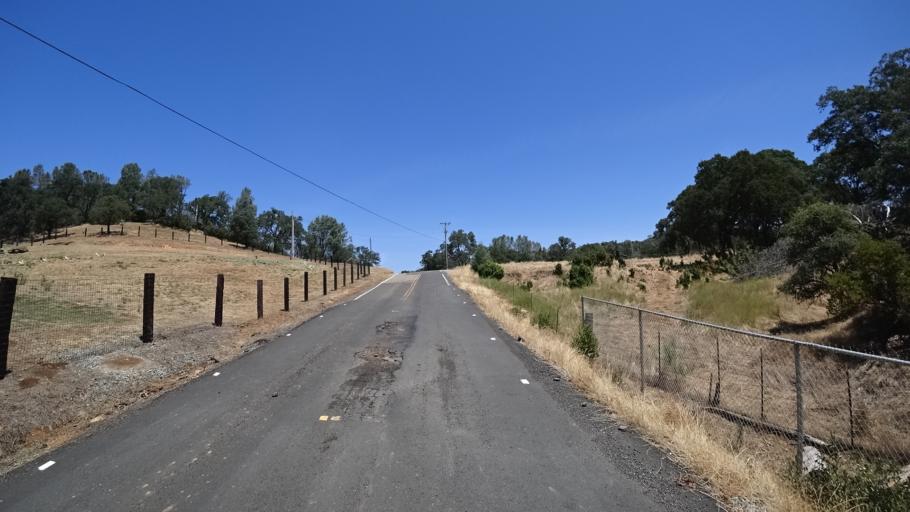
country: US
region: California
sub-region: Calaveras County
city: Valley Springs
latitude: 38.2101
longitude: -120.8626
